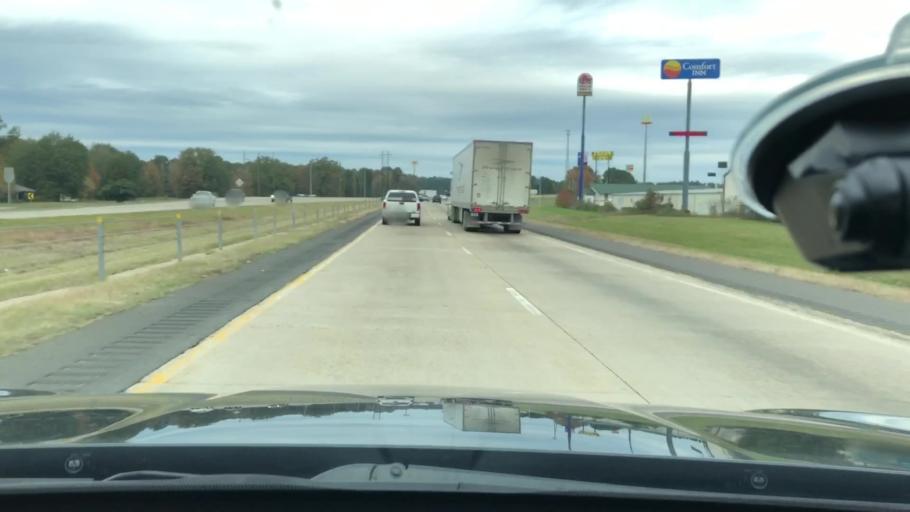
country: US
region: Arkansas
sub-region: Clark County
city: Arkadelphia
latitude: 34.1794
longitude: -93.0734
